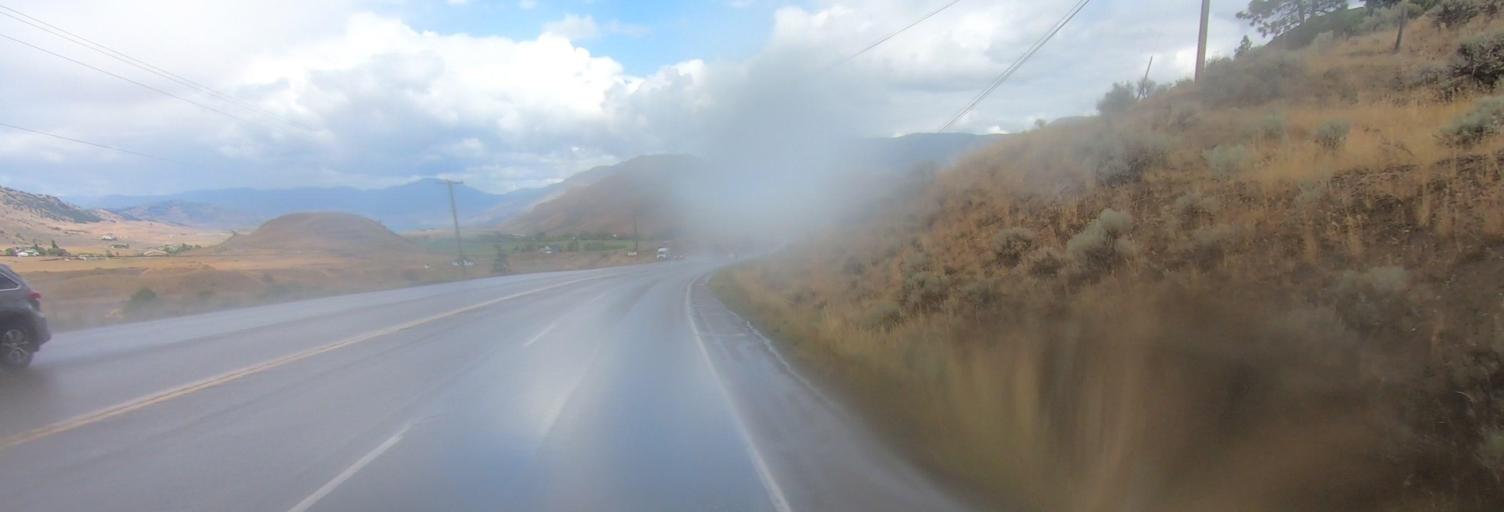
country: CA
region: British Columbia
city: Kamloops
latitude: 50.6875
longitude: -120.5838
